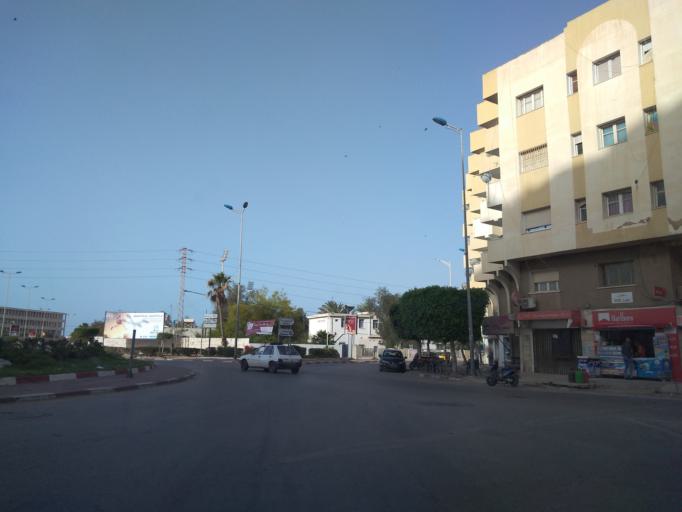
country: TN
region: Safaqis
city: Sfax
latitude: 34.7358
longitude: 10.7486
